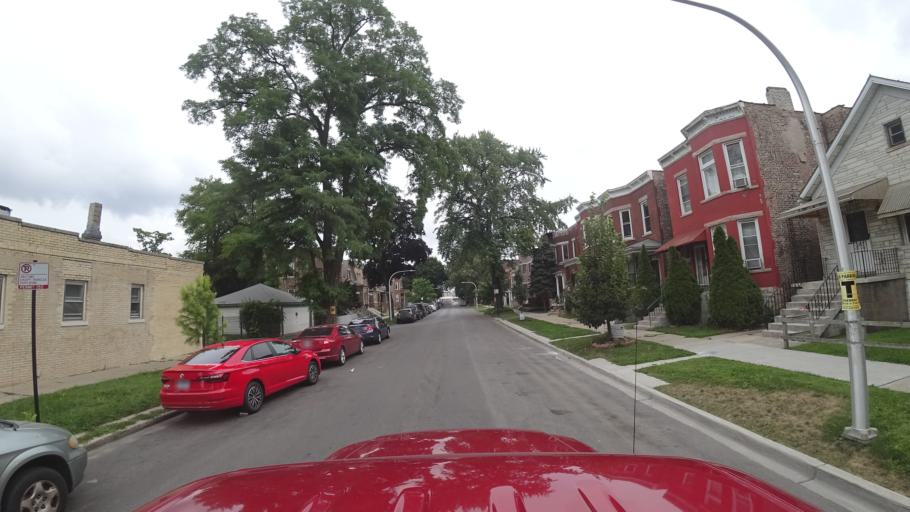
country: US
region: Illinois
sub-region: Cook County
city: Chicago
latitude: 41.8268
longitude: -87.6801
